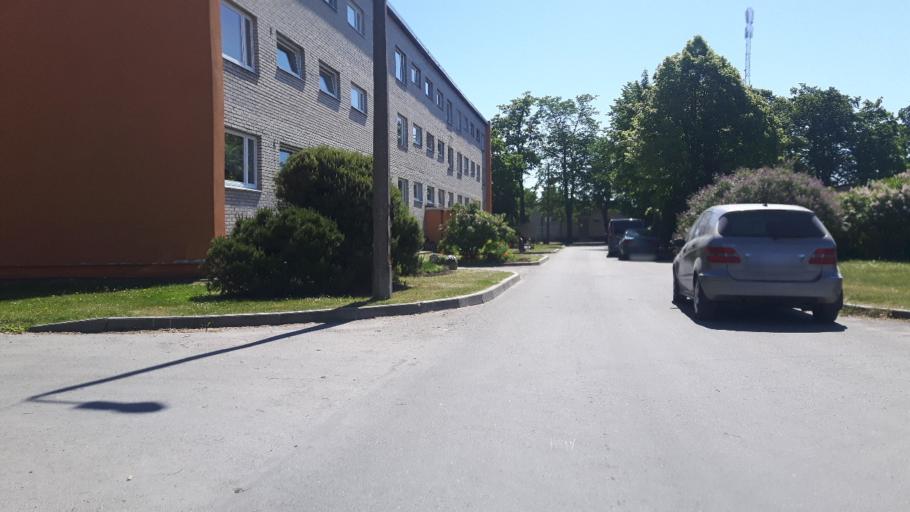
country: EE
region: Harju
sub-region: Saku vald
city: Saku
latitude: 59.2971
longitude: 24.6641
